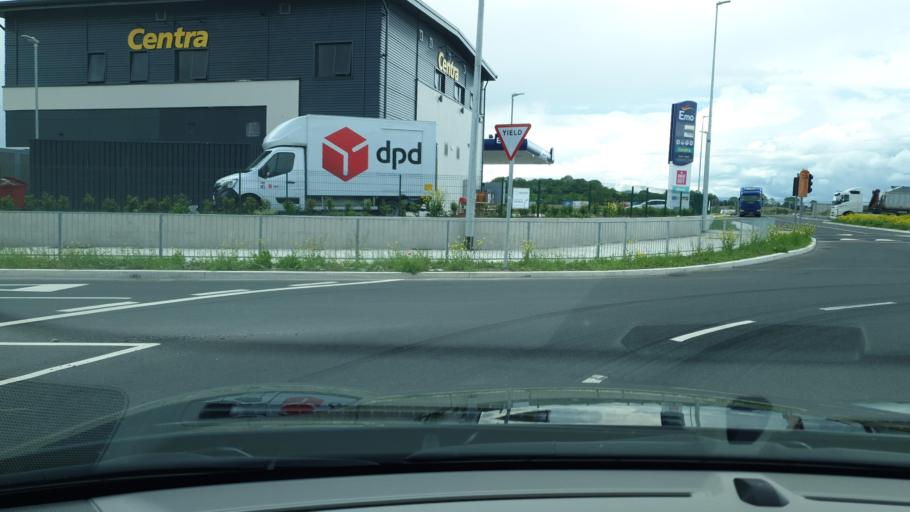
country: IE
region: Leinster
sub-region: Kildare
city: Kildare
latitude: 53.1496
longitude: -6.9189
